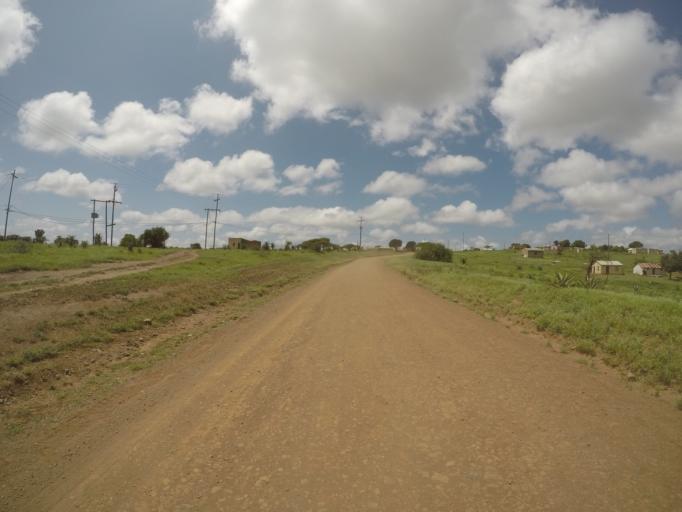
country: ZA
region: KwaZulu-Natal
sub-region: uThungulu District Municipality
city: Empangeni
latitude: -28.5766
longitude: 31.8403
